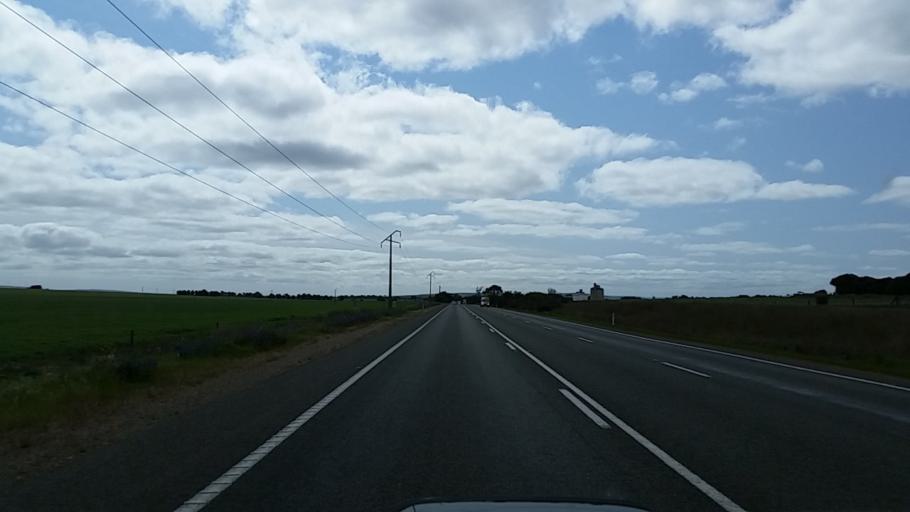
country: AU
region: South Australia
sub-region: Port Pirie City and Dists
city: Crystal Brook
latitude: -33.5587
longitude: 138.2232
